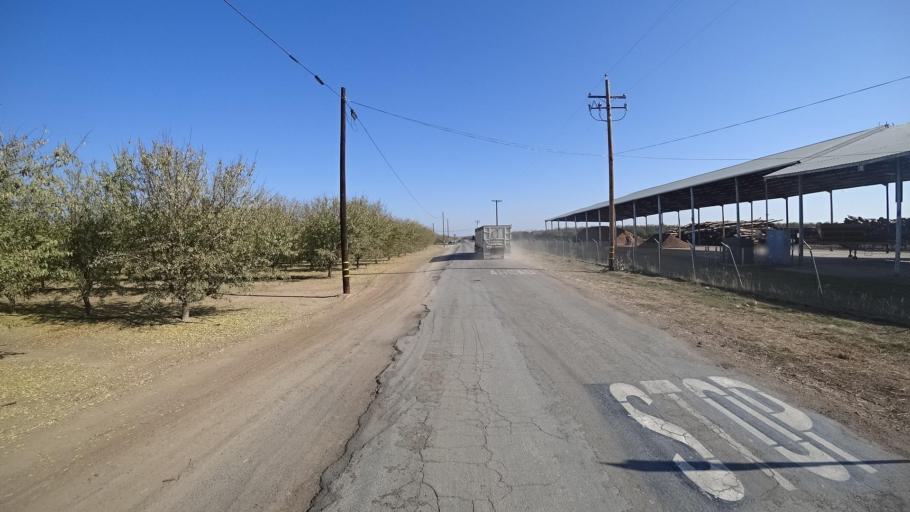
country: US
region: California
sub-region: Kern County
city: McFarland
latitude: 35.6451
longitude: -119.2025
